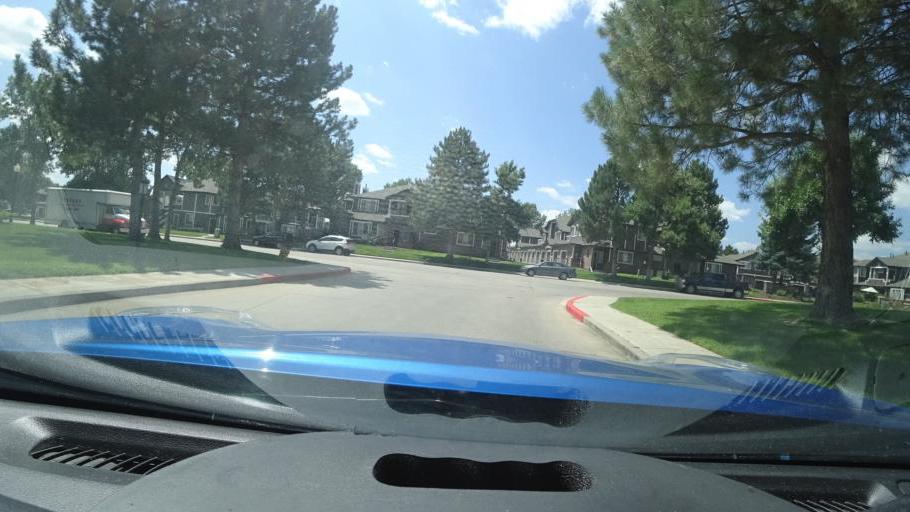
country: US
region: Colorado
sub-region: Arapahoe County
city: Glendale
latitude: 39.6986
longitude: -104.8876
